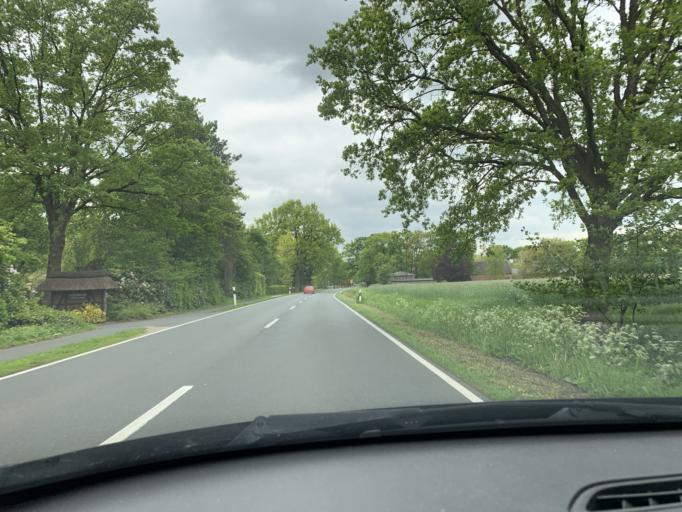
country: DE
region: Lower Saxony
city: Bad Zwischenahn
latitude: 53.1903
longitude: 8.0567
